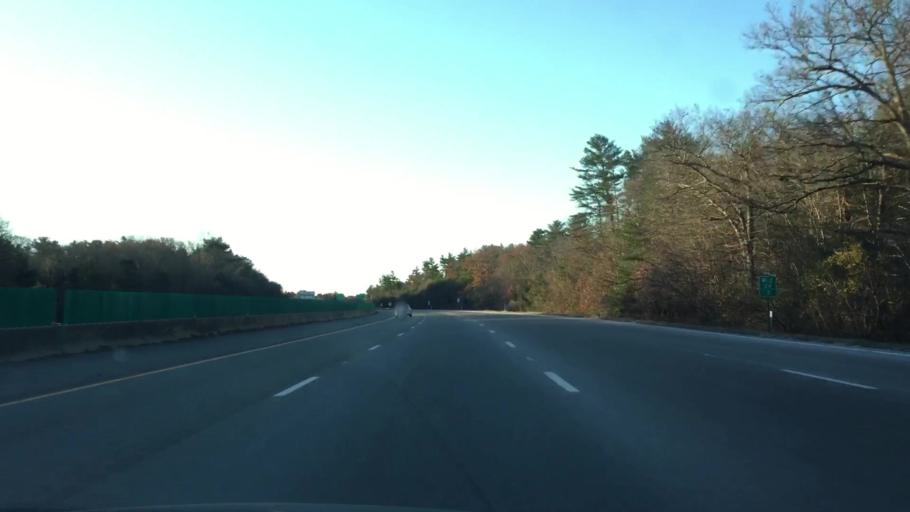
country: US
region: Massachusetts
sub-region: Bristol County
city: Raynham
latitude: 41.9653
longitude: -71.0281
